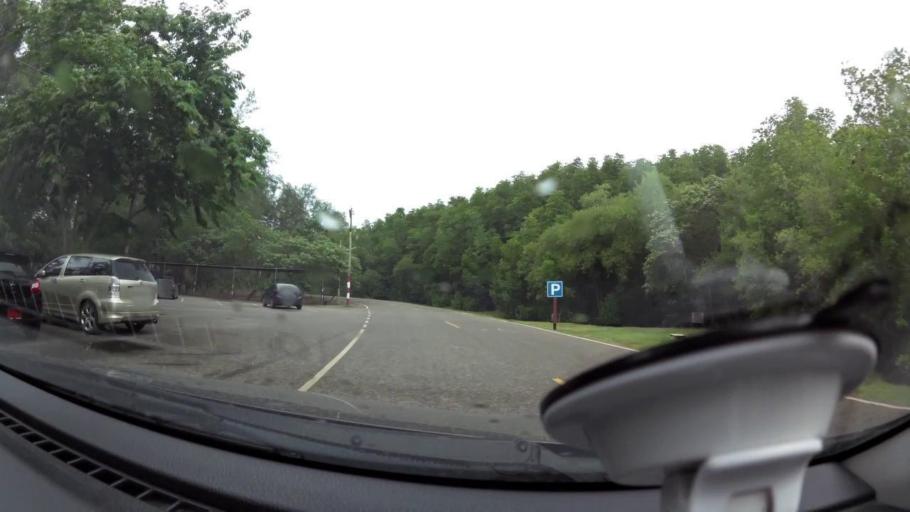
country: TH
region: Prachuap Khiri Khan
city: Pran Buri
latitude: 12.4134
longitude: 99.9853
